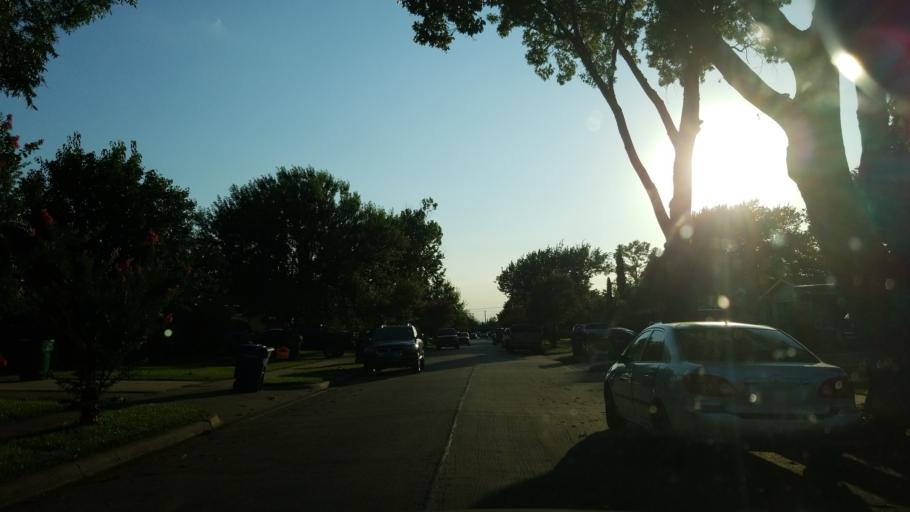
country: US
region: Texas
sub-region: Dallas County
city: Carrollton
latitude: 32.9441
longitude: -96.8961
